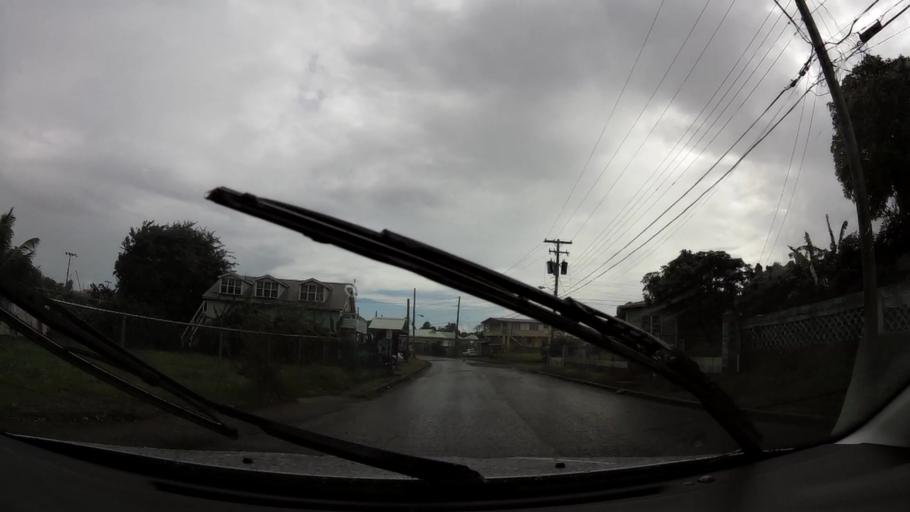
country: AG
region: Saint John
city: Saint John's
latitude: 17.1111
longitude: -61.8386
